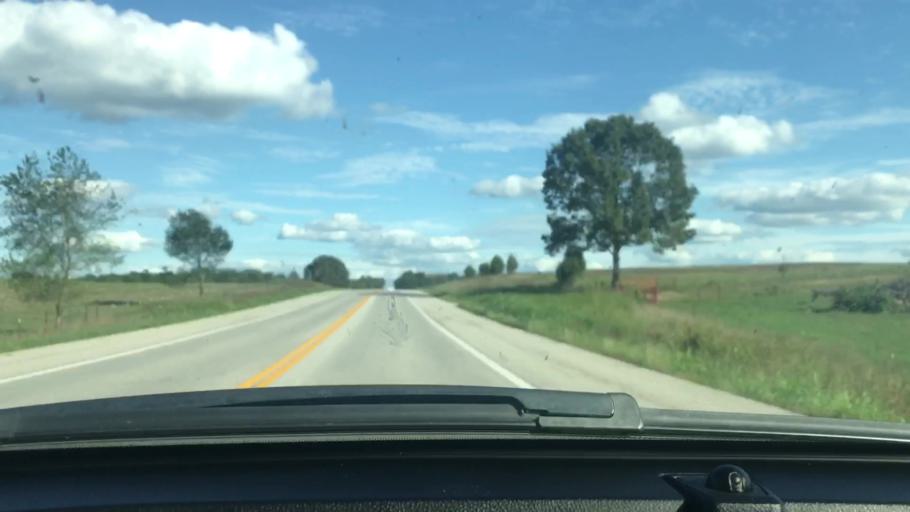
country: US
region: Missouri
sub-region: Howell County
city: West Plains
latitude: 36.6572
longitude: -91.7017
